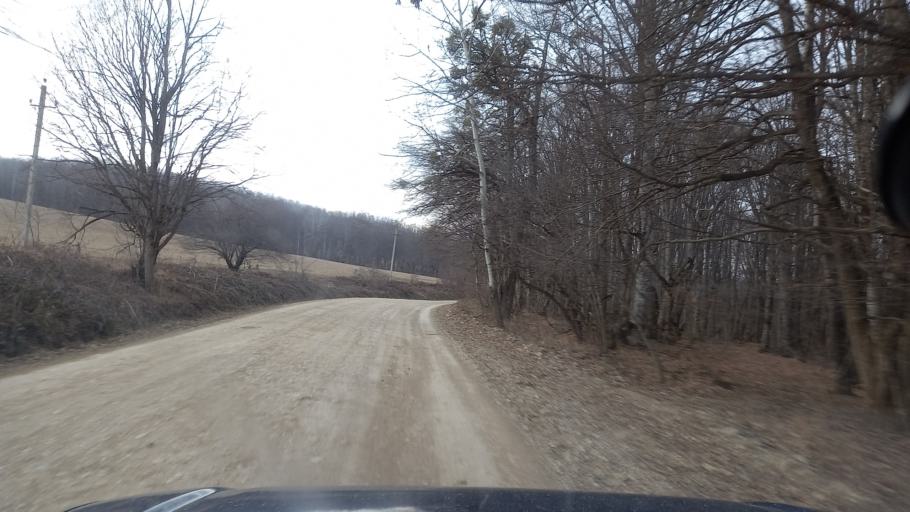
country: RU
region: Adygeya
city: Kamennomostskiy
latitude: 44.1468
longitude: 40.2504
